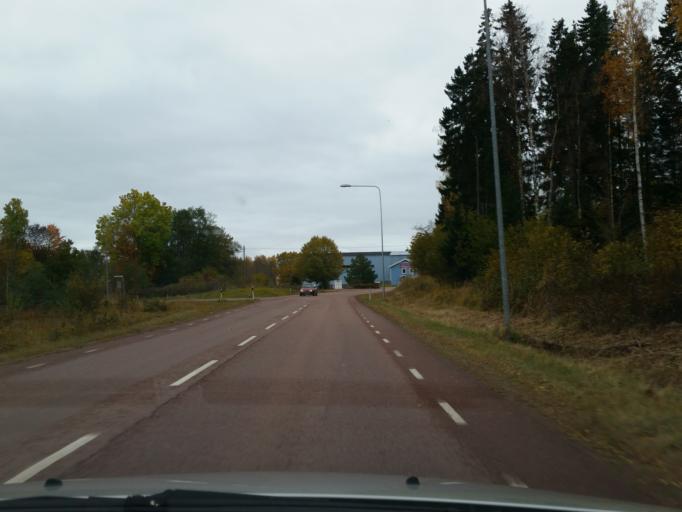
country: AX
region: Mariehamns stad
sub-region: Mariehamn
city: Mariehamn
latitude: 60.1107
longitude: 19.9139
